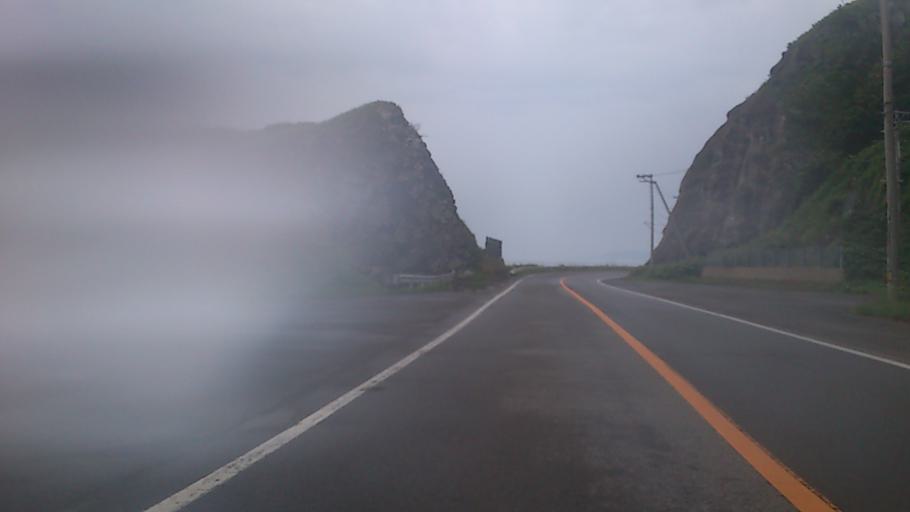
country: JP
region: Akita
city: Noshiromachi
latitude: 40.4450
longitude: 139.9400
